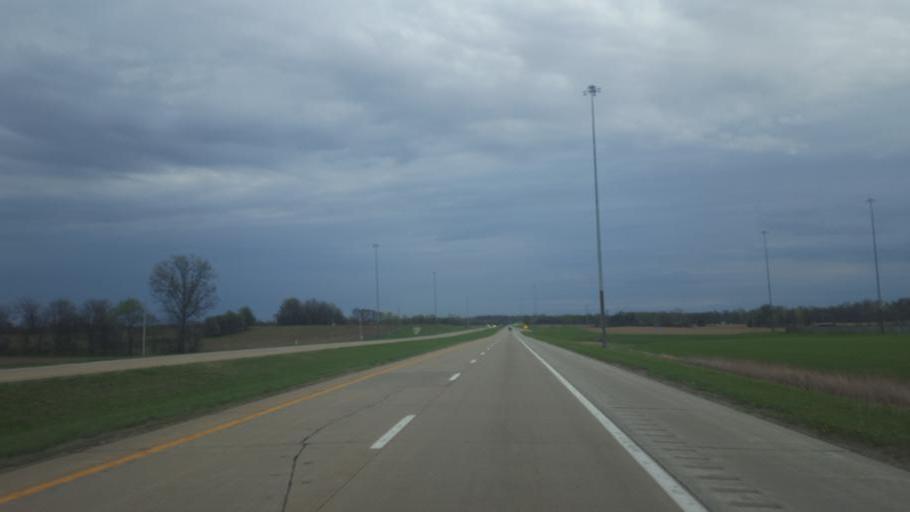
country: US
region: Ohio
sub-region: Wyandot County
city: Upper Sandusky
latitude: 40.8078
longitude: -83.1715
